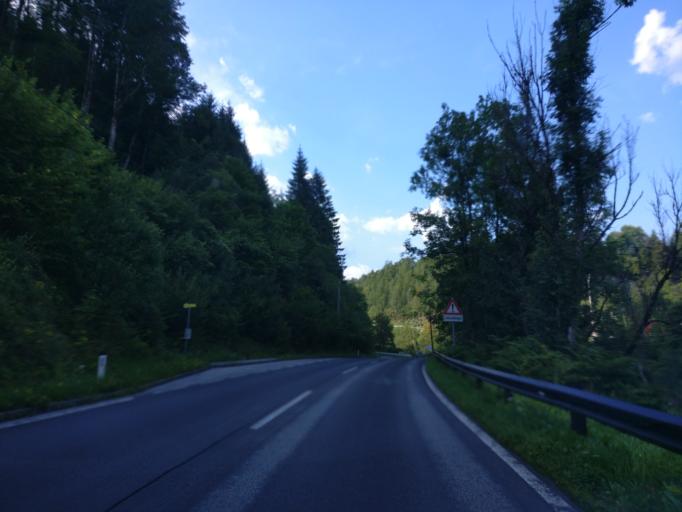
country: AT
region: Styria
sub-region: Politischer Bezirk Liezen
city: Gams bei Hieflau
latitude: 47.6344
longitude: 14.7593
